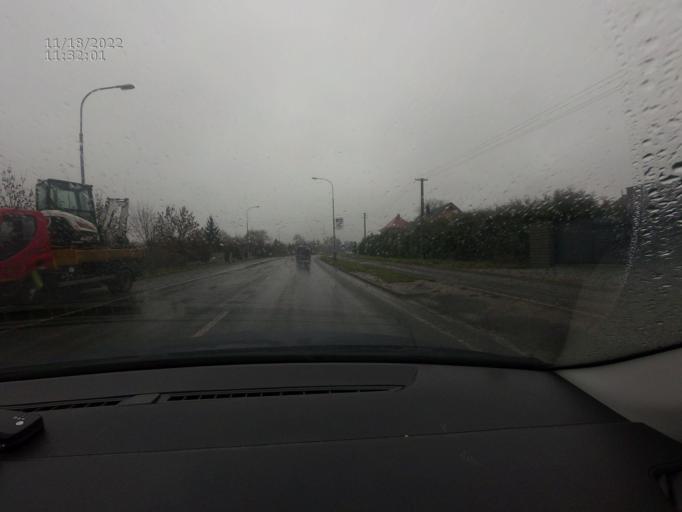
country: CZ
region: Plzensky
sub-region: Okres Rokycany
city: Rokycany
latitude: 49.7353
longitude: 13.5861
